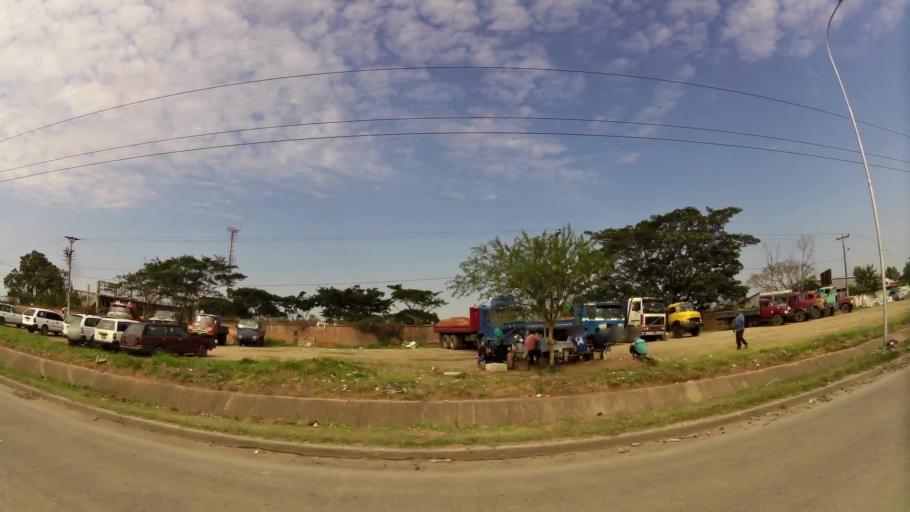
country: BO
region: Santa Cruz
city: Santa Cruz de la Sierra
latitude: -17.7479
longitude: -63.1517
